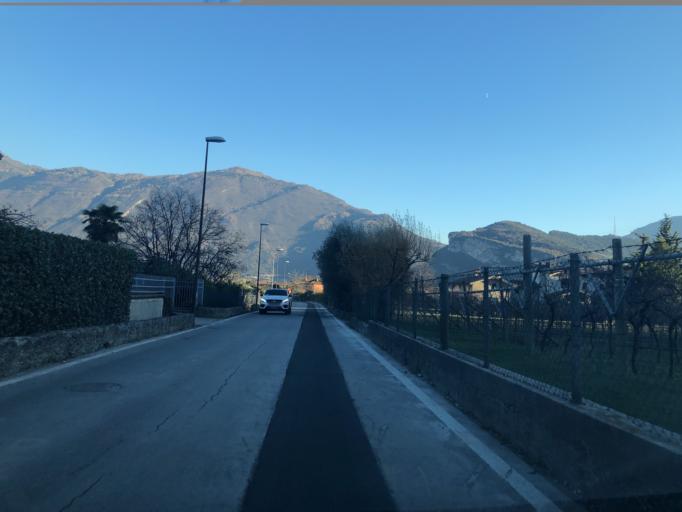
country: IT
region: Trentino-Alto Adige
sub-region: Provincia di Trento
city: Riva del Garda
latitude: 45.9043
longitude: 10.8541
